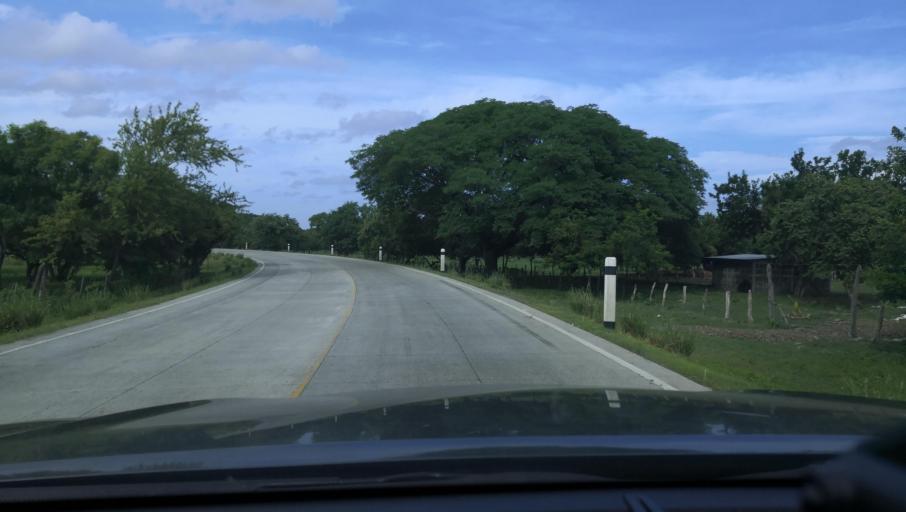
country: NI
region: Boaco
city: San Lorenzo
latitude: 12.1844
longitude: -85.7308
